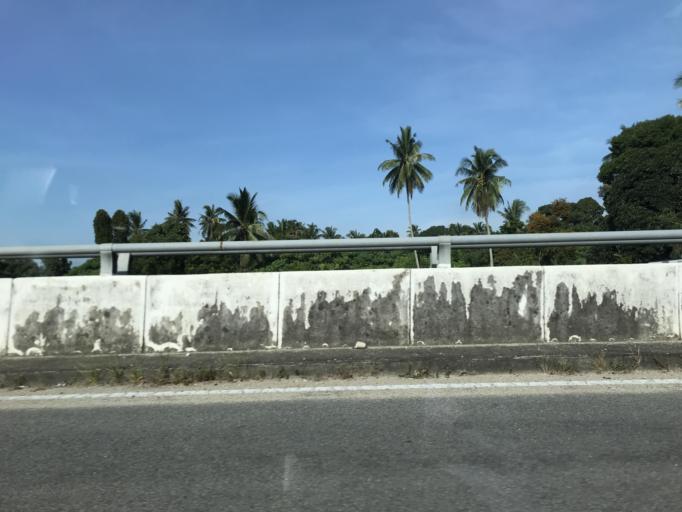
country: MY
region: Kelantan
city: Kampong Kadok
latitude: 6.0593
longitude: 102.2107
